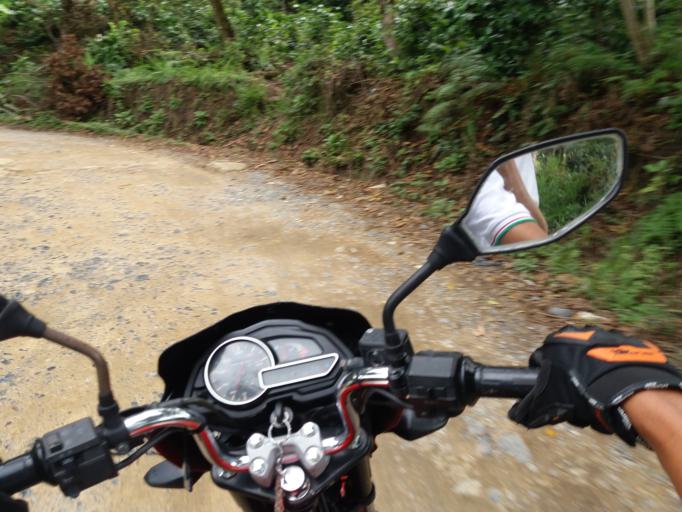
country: CO
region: Santander
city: Guepsa
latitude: 6.0097
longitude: -73.5474
